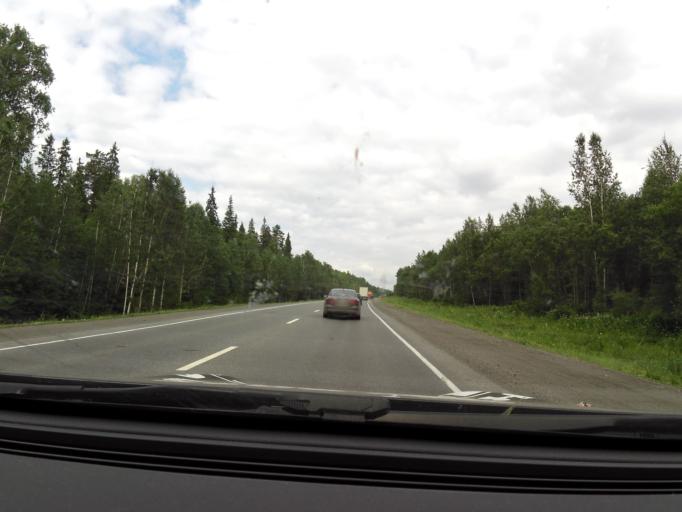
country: RU
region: Sverdlovsk
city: Bilimbay
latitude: 56.8508
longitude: 59.6932
